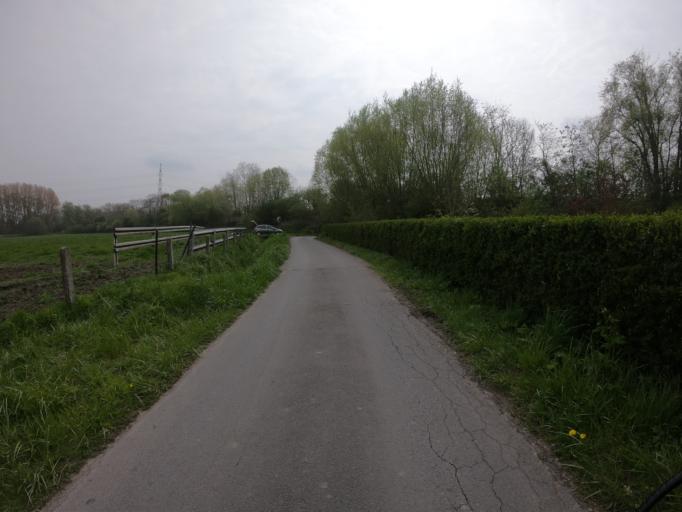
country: BE
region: Flanders
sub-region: Provincie West-Vlaanderen
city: Avelgem
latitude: 50.7608
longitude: 3.4589
